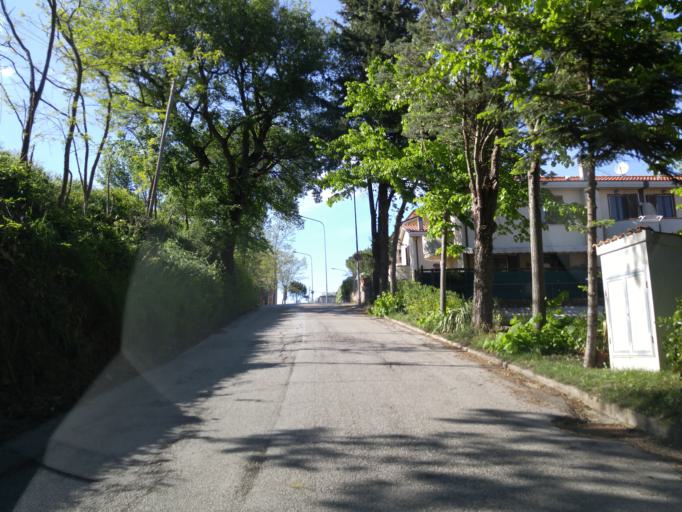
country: IT
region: The Marches
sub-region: Provincia di Pesaro e Urbino
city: Mombaroccio
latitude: 43.8101
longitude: 12.8495
